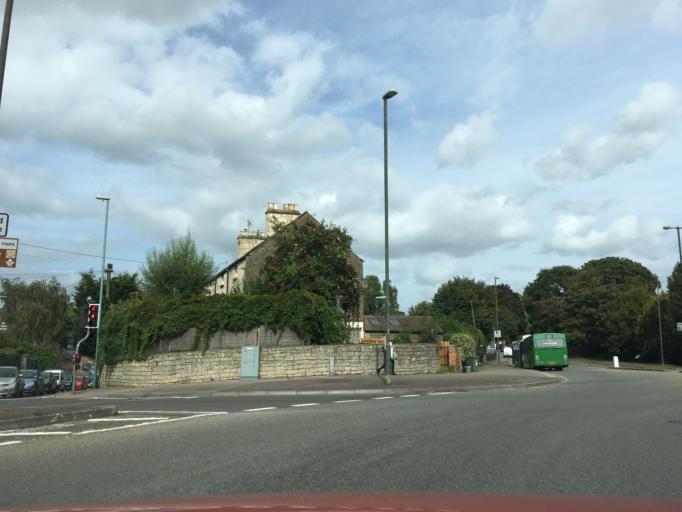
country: GB
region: England
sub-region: Gloucestershire
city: Stroud
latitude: 51.7439
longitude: -2.2400
